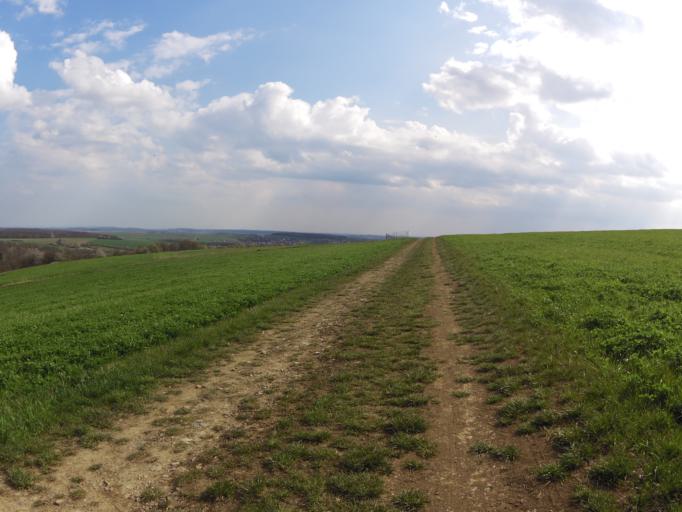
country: DE
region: Bavaria
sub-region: Regierungsbezirk Unterfranken
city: Rimpar
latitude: 49.8725
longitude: 9.9601
